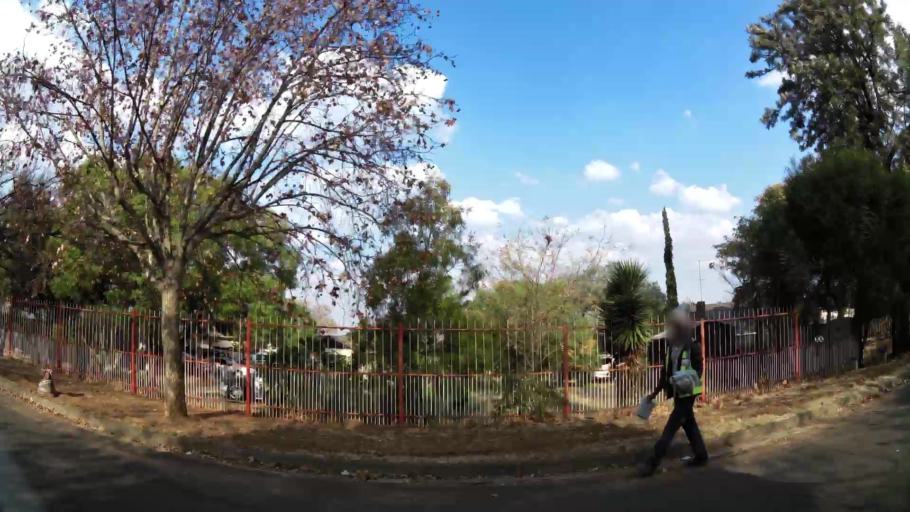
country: ZA
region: Gauteng
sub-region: Ekurhuleni Metropolitan Municipality
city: Germiston
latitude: -26.2436
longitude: 28.1855
